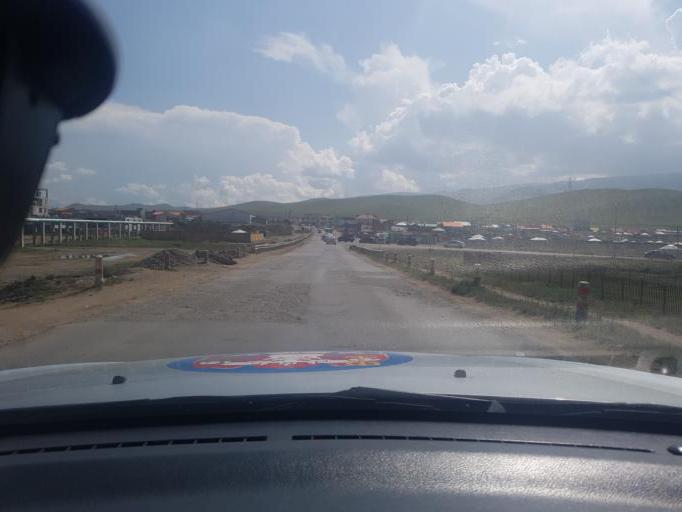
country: MN
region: Ulaanbaatar
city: Ulaanbaatar
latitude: 47.8917
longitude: 107.0665
